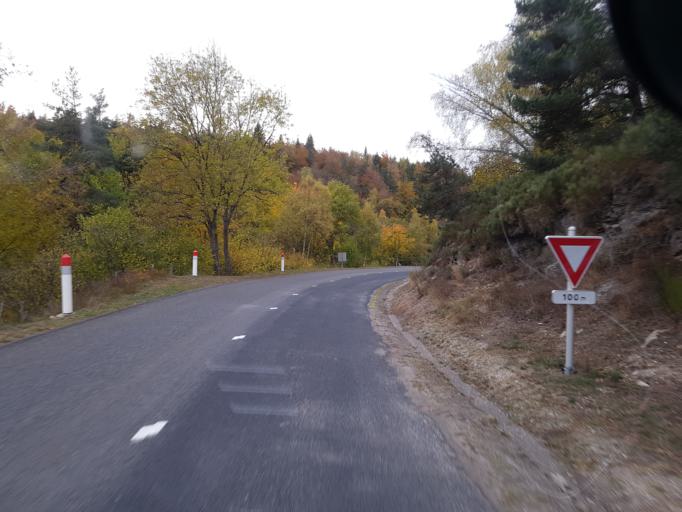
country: FR
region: Languedoc-Roussillon
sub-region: Departement de la Lozere
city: Langogne
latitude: 44.7242
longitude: 3.7482
